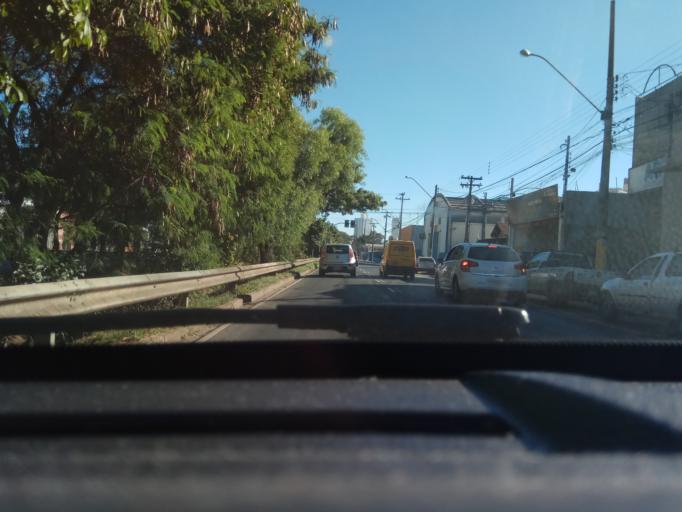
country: BR
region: Sao Paulo
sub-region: Piracicaba
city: Piracicaba
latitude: -22.7427
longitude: -47.6455
